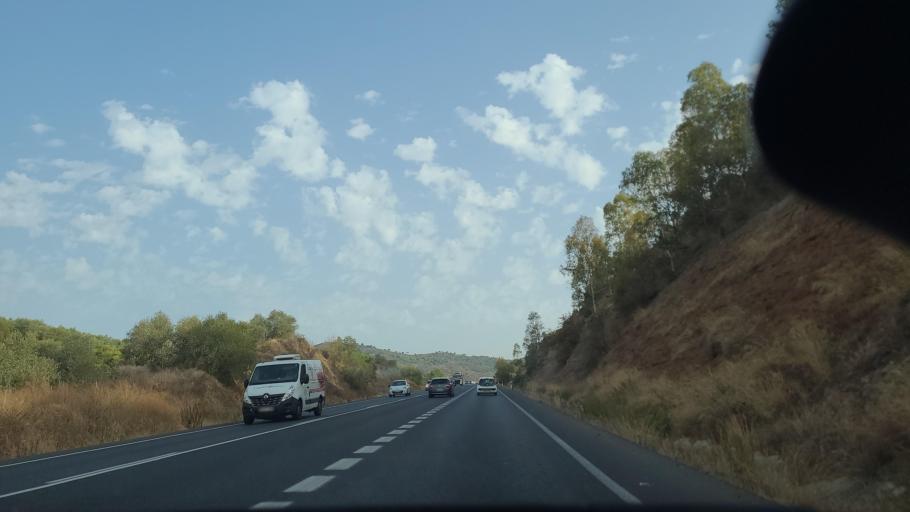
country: ES
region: Andalusia
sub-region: Province of Cordoba
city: Cordoba
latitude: 37.9595
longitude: -4.7667
